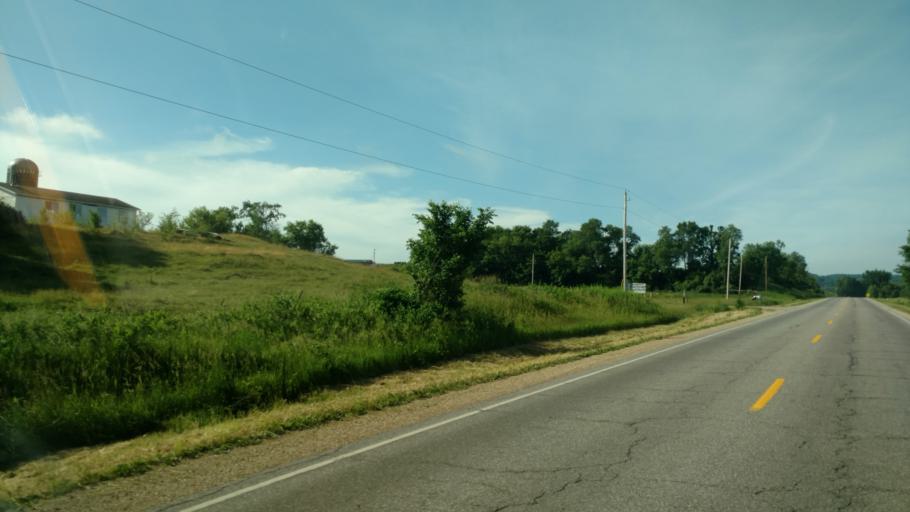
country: US
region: Wisconsin
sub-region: Sauk County
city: Reedsburg
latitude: 43.5594
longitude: -90.1340
